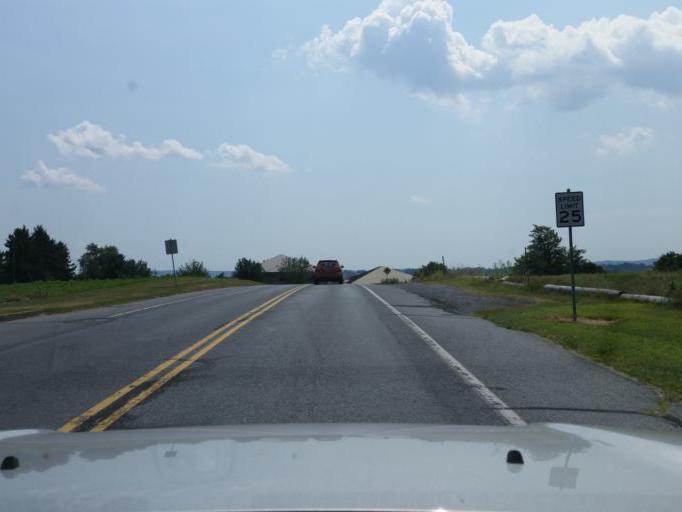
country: US
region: Pennsylvania
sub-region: Dauphin County
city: Lawnton
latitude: 40.2653
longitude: -76.8084
